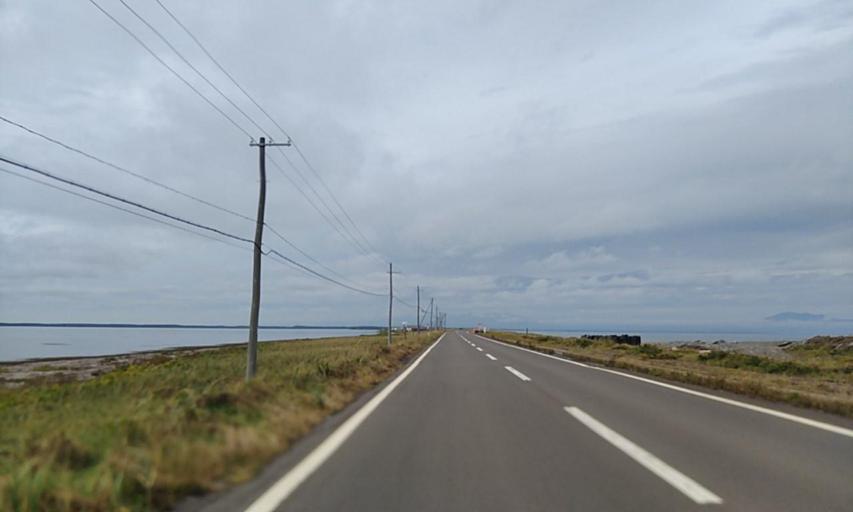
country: JP
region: Hokkaido
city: Shibetsu
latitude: 43.6109
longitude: 145.2665
